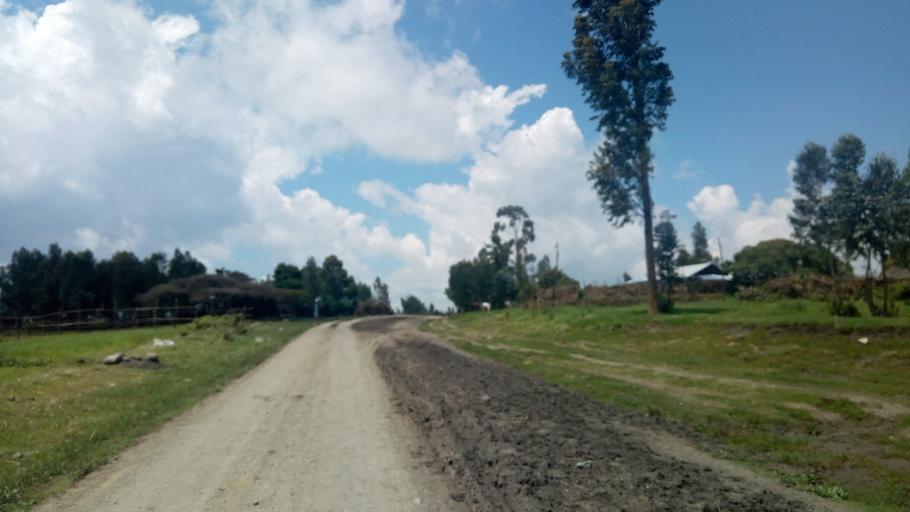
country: ET
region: Oromiya
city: Sendafa
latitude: 8.9957
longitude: 39.1260
